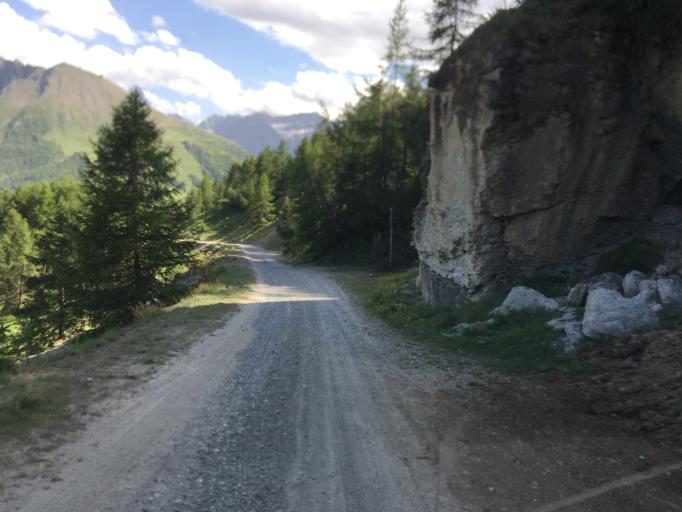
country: IT
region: Piedmont
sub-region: Provincia di Torino
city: Sestriere
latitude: 44.9732
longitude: 6.8822
